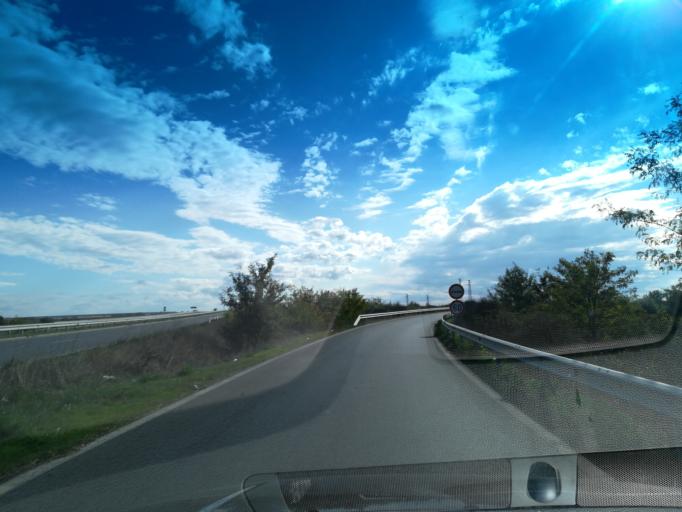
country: BG
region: Stara Zagora
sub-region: Obshtina Stara Zagora
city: Stara Zagora
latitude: 42.3423
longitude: 25.6609
